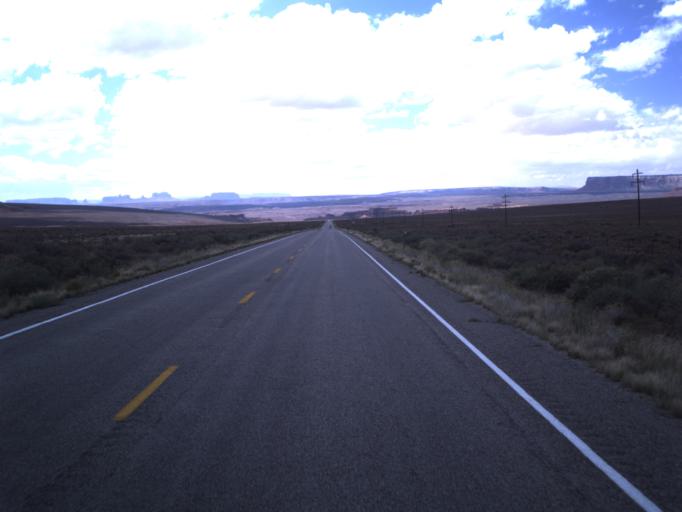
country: US
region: Utah
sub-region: San Juan County
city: Blanding
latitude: 37.2546
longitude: -109.7496
